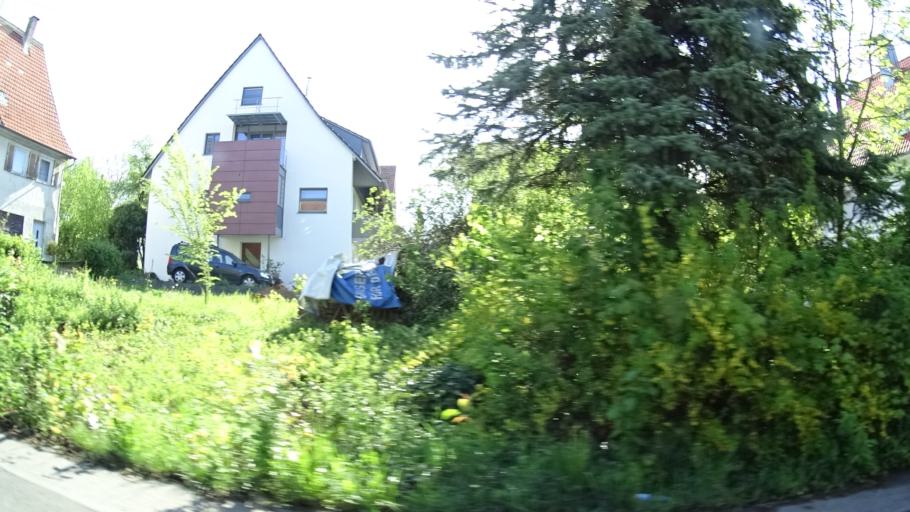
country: DE
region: Baden-Wuerttemberg
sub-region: Regierungsbezirk Stuttgart
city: Motzingen
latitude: 48.5051
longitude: 8.7770
